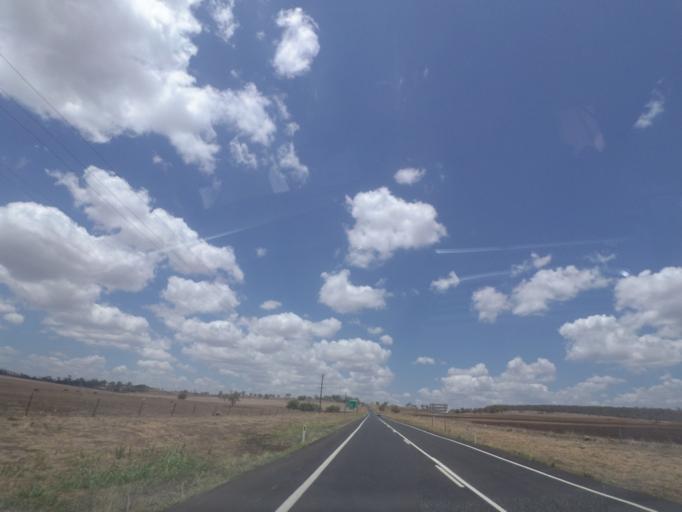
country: AU
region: Queensland
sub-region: Toowoomba
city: Top Camp
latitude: -27.7206
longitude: 151.9116
